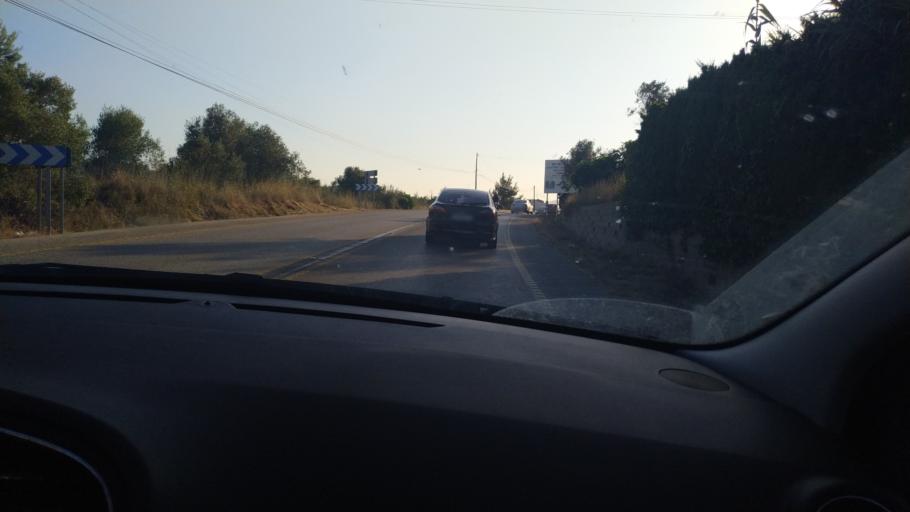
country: ES
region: Valencia
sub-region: Provincia de Alicante
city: Javea
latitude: 38.7754
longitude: 0.1439
